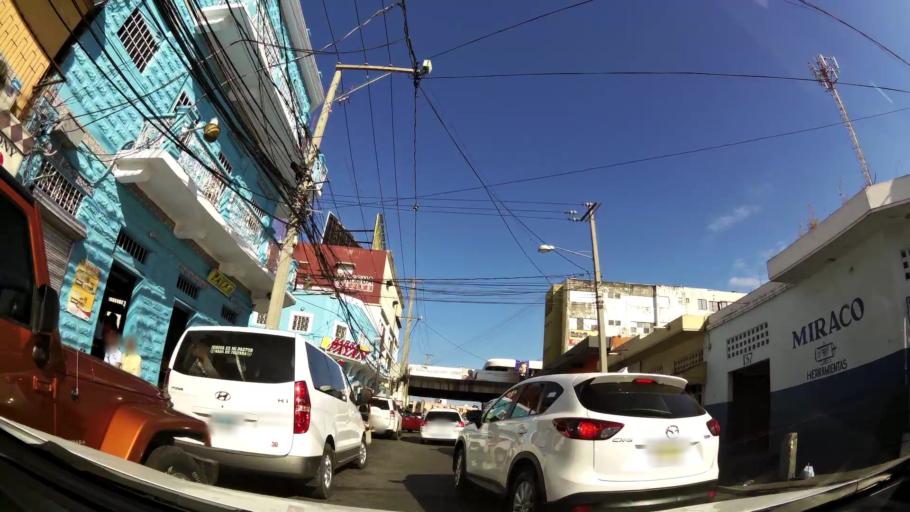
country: DO
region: Nacional
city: San Carlos
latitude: 18.4786
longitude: -69.8985
